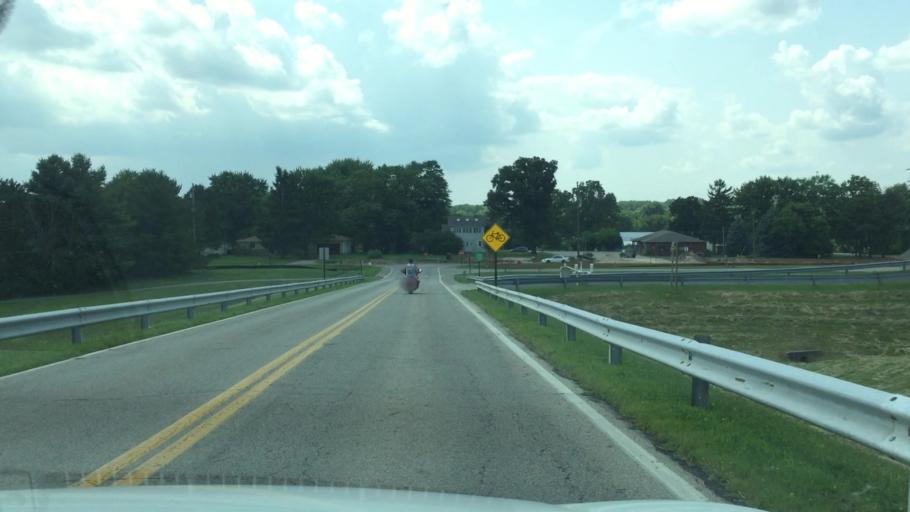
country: US
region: Ohio
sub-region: Clark County
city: Northridge
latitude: 39.9472
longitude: -83.7465
